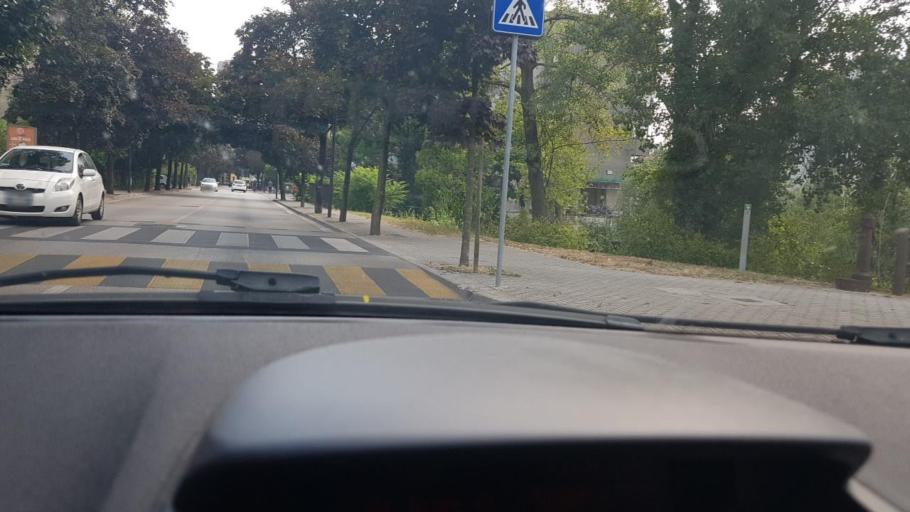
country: IT
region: Friuli Venezia Giulia
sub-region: Provincia di Pordenone
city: Pordenone
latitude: 45.9615
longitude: 12.6671
